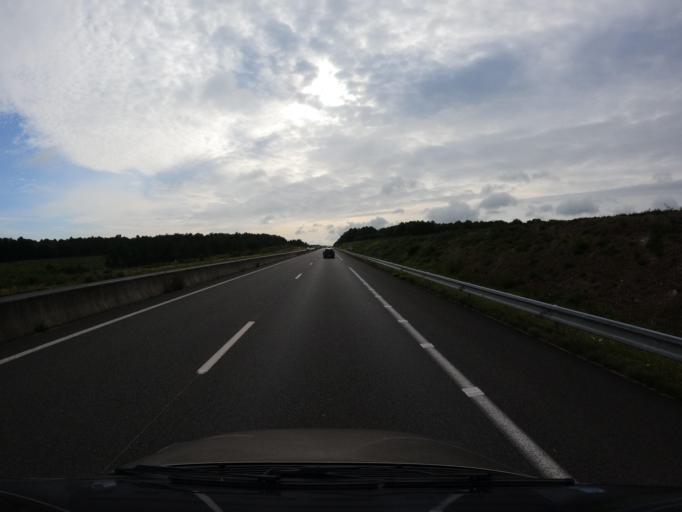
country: FR
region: Centre
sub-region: Departement d'Indre-et-Loire
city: Langeais
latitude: 47.3467
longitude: 0.3760
